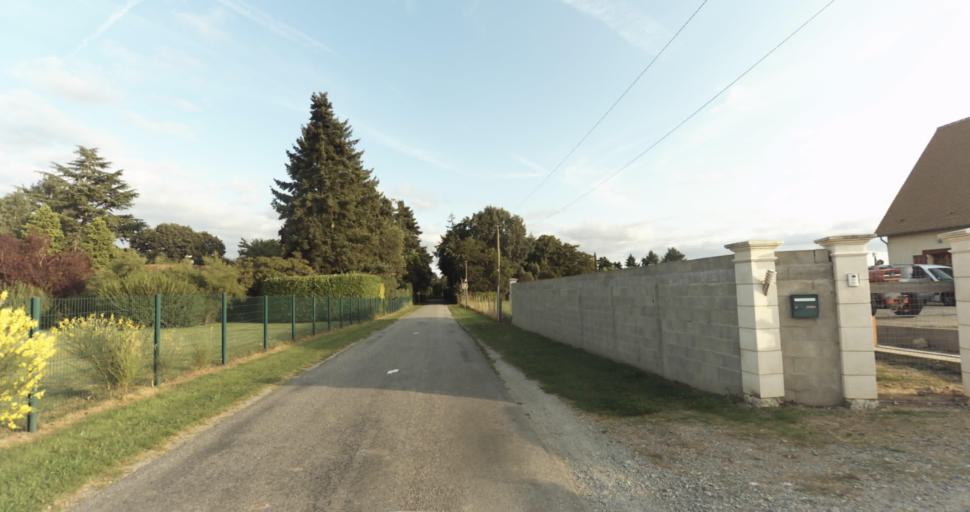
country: FR
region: Haute-Normandie
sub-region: Departement de l'Eure
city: Marcilly-sur-Eure
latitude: 48.8392
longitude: 1.2802
